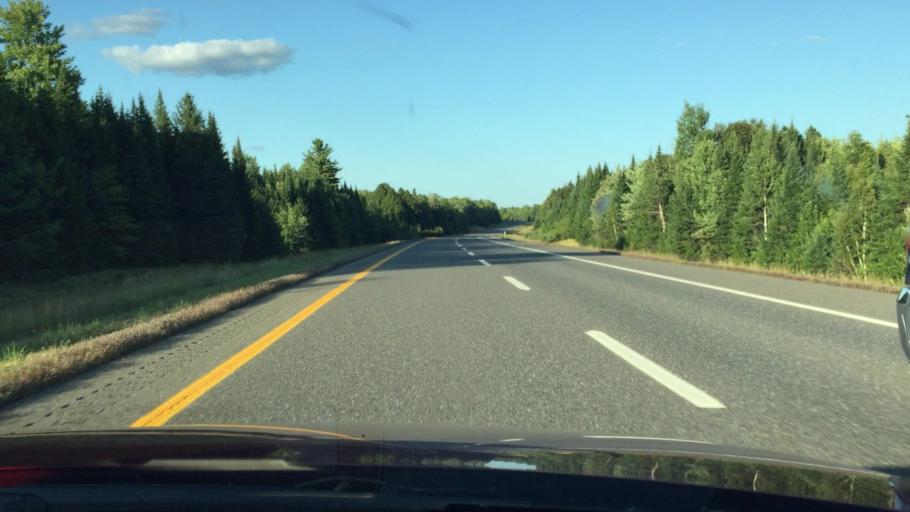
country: US
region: Maine
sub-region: Penobscot County
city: Patten
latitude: 46.0440
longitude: -68.2578
